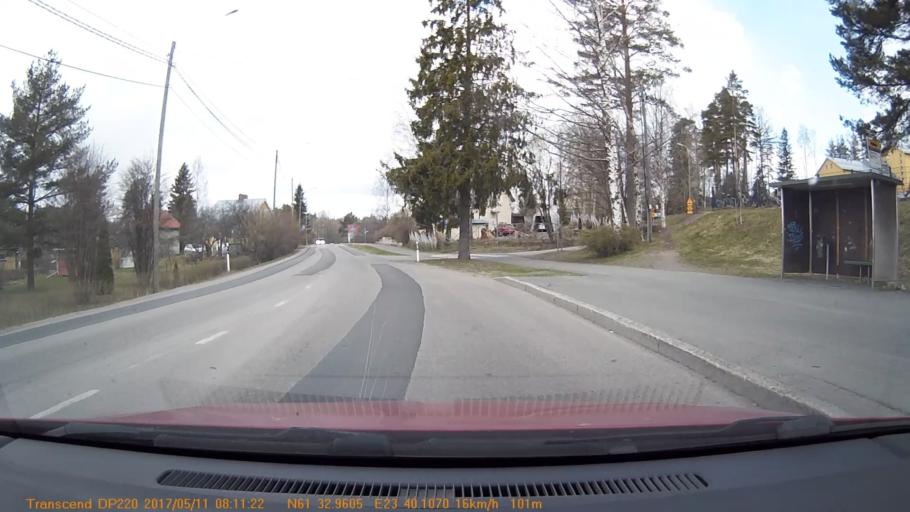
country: FI
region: Pirkanmaa
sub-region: Tampere
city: Yloejaervi
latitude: 61.5493
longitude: 23.6685
